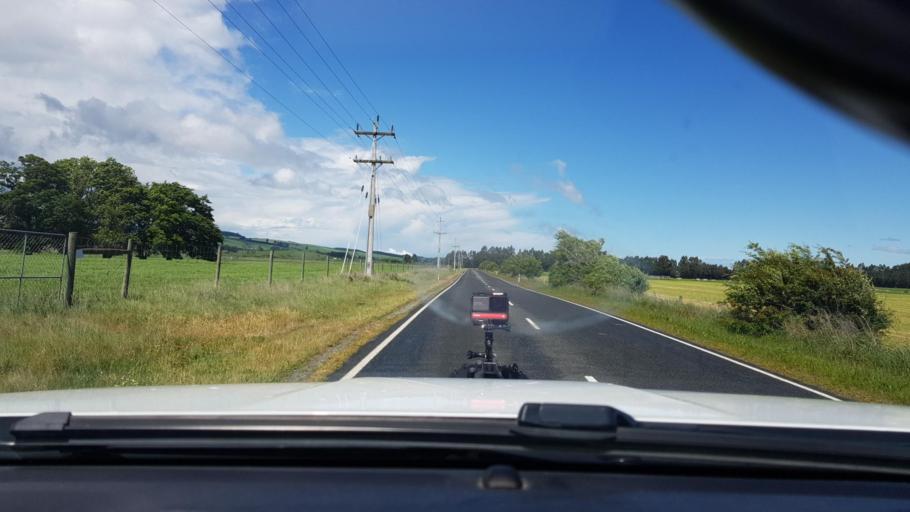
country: NZ
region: Southland
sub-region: Southland District
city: Winton
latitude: -45.8670
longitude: 168.3581
